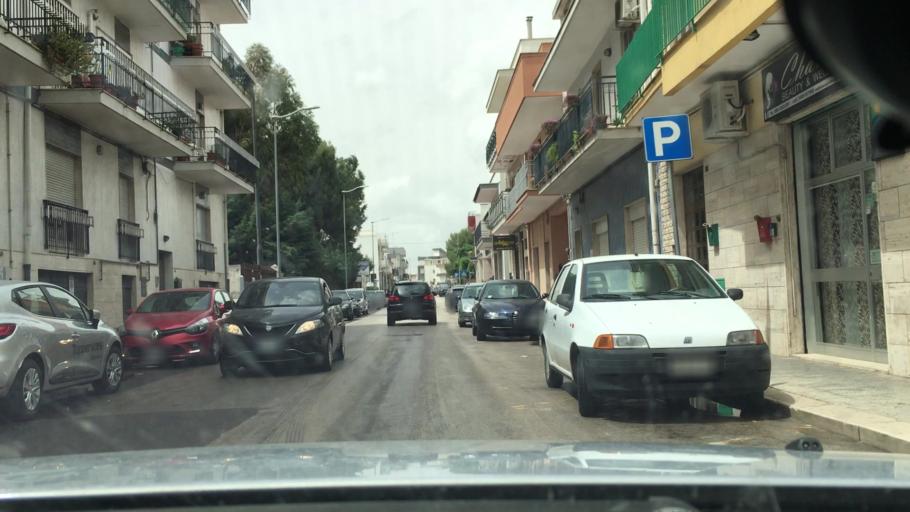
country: IT
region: Apulia
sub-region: Provincia di Bari
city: Capurso
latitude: 41.0498
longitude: 16.9205
